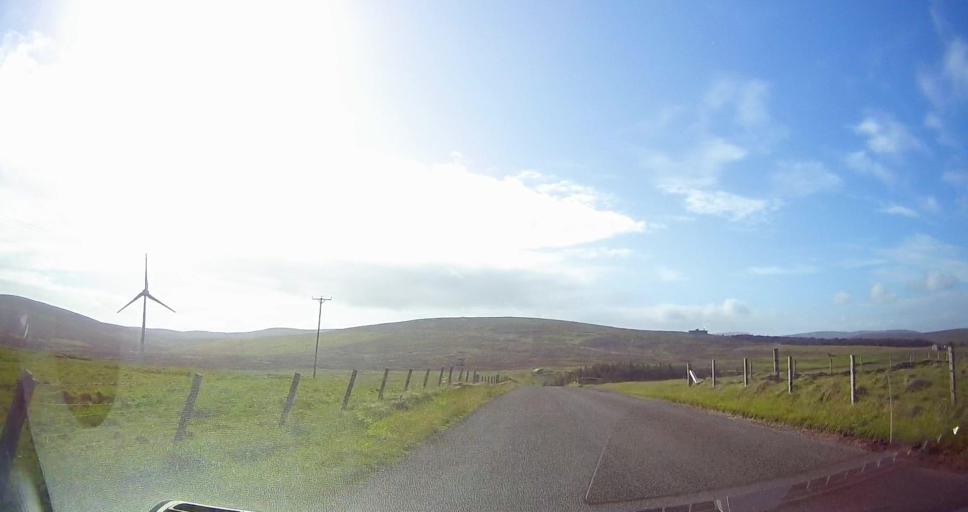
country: GB
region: Scotland
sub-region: Orkney Islands
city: Stromness
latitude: 58.8230
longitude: -3.2073
